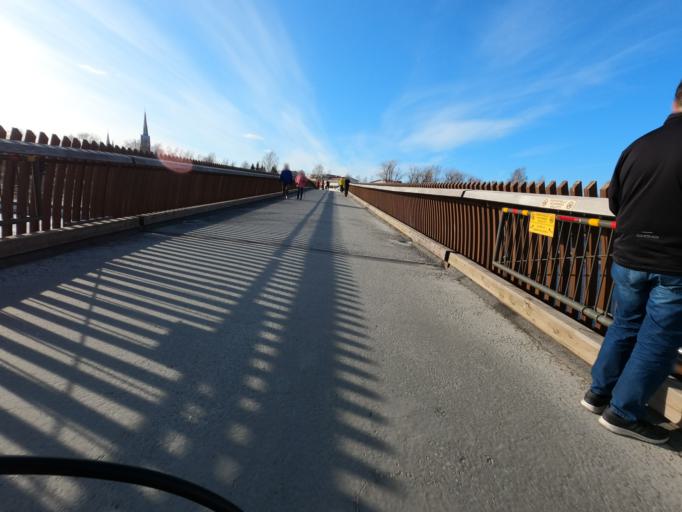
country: FI
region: North Karelia
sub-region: Joensuu
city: Joensuu
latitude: 62.5936
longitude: 29.7591
